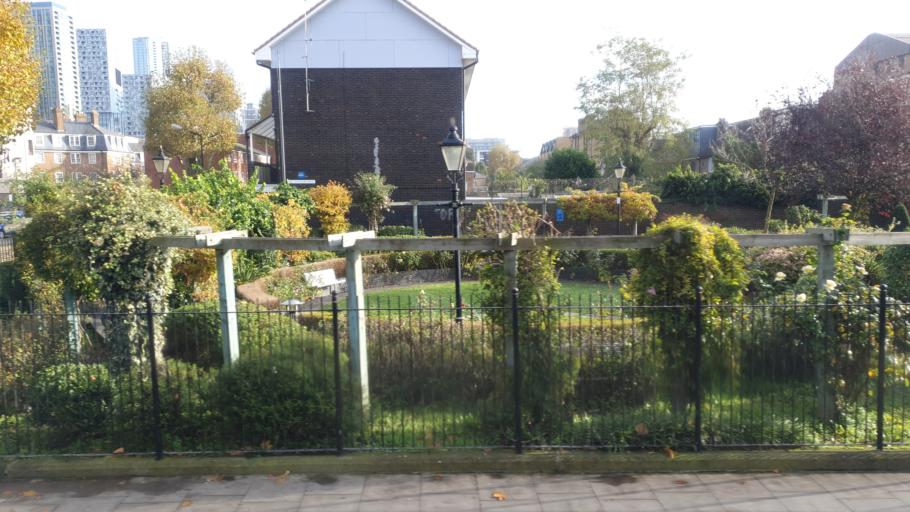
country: GB
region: England
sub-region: Greater London
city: Poplar
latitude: 51.4966
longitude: -0.0257
